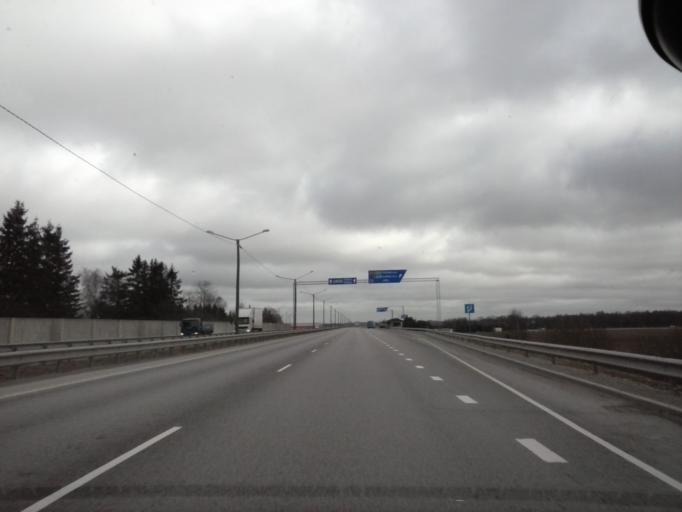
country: EE
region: Harju
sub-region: Rae vald
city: Jueri
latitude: 59.3584
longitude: 24.8743
